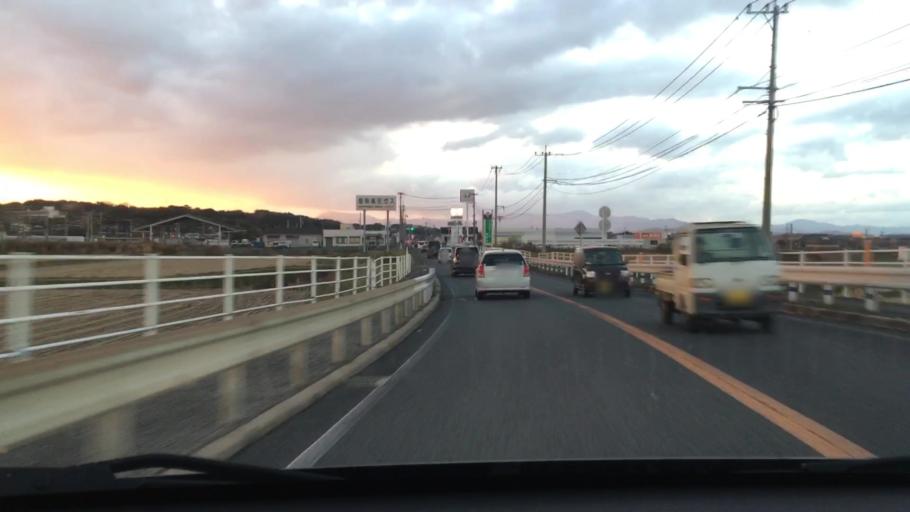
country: JP
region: Fukuoka
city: Shiida
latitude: 33.6286
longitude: 131.0869
